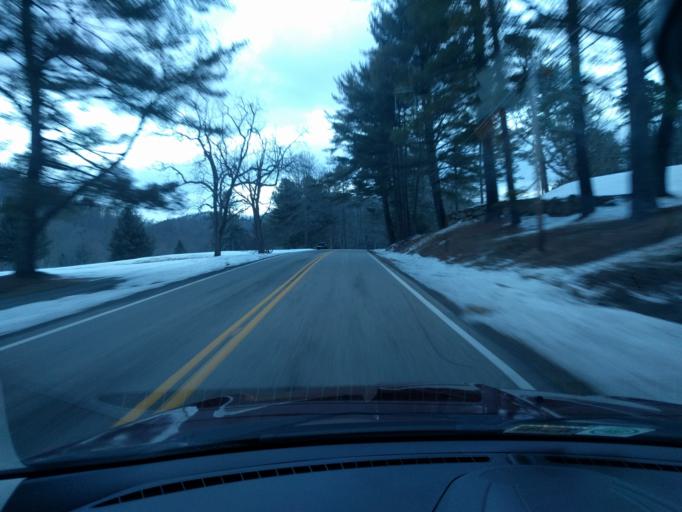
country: US
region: Virginia
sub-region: Bath County
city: Warm Springs
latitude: 37.9498
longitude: -79.8699
